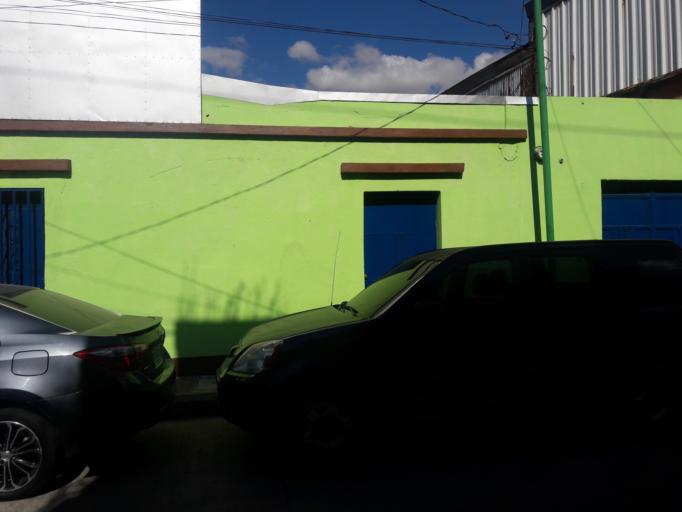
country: GT
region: Guatemala
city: Amatitlan
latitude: 14.4817
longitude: -90.6195
